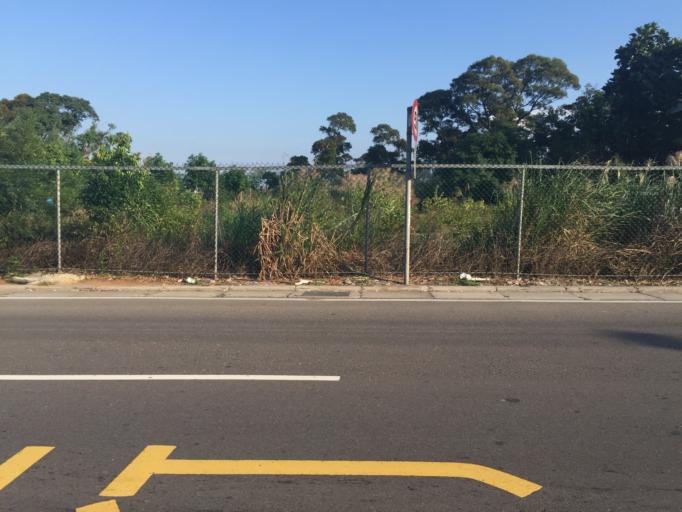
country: TW
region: Taiwan
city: Daxi
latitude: 24.9268
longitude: 121.2591
